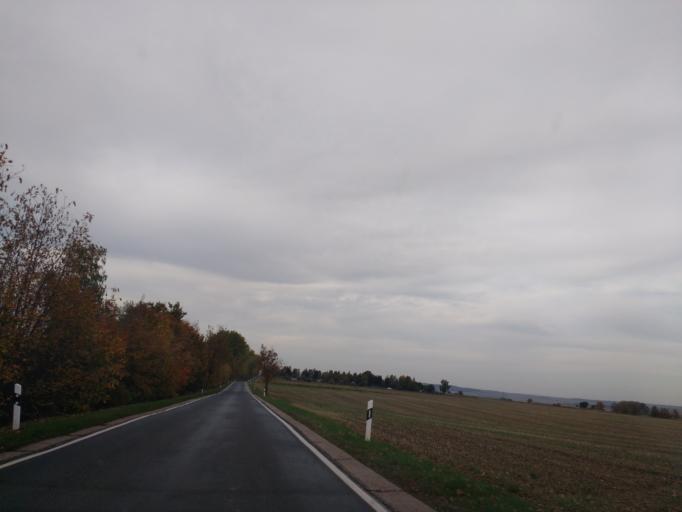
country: DE
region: Thuringia
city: Seebach
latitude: 51.1714
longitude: 10.5103
